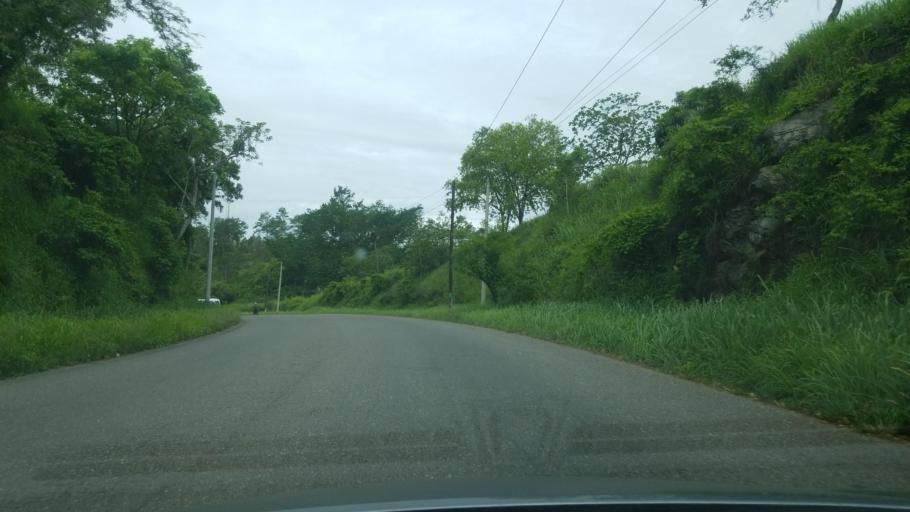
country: HN
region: Santa Barbara
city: San Marcos
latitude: 15.3042
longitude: -88.4531
